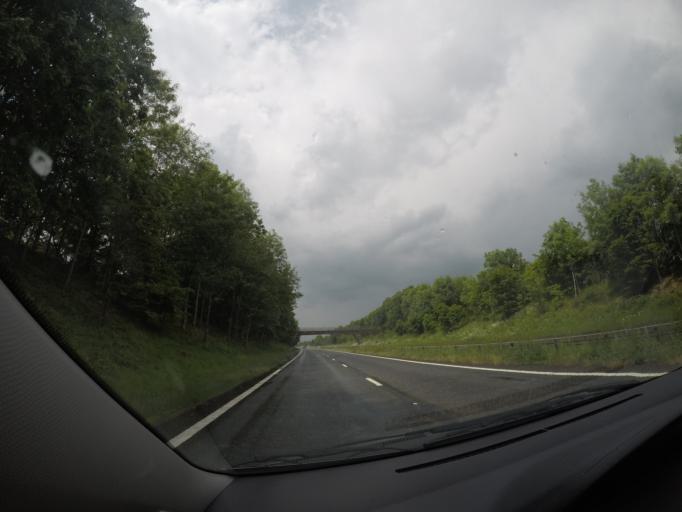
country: GB
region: England
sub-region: Cumbria
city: Appleby-in-Westmorland
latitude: 54.5779
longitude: -2.4726
